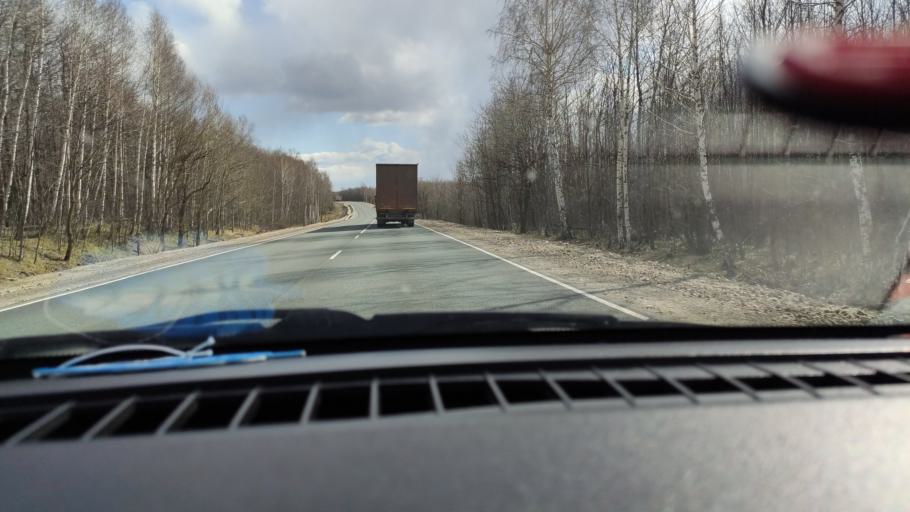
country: RU
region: Saratov
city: Khvalynsk
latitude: 52.4778
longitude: 48.0133
